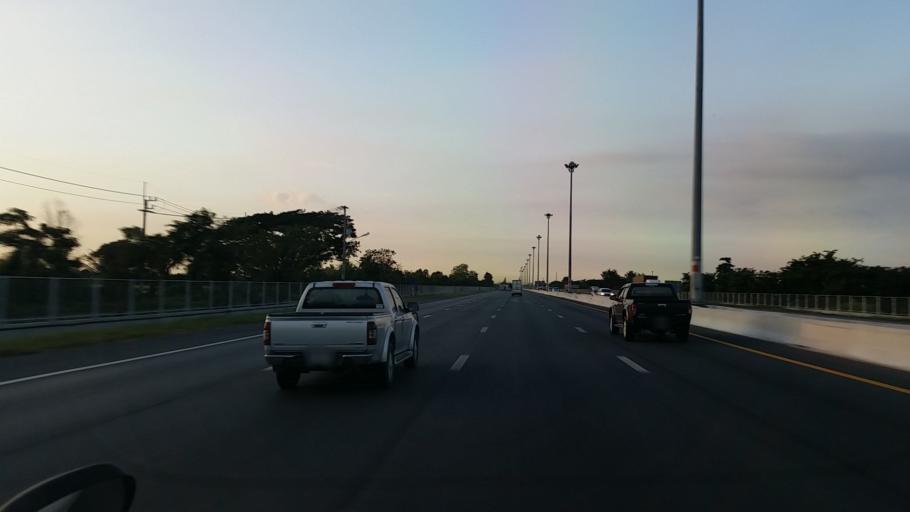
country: TH
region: Pathum Thani
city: Khlong Luang
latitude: 14.1514
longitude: 100.6581
